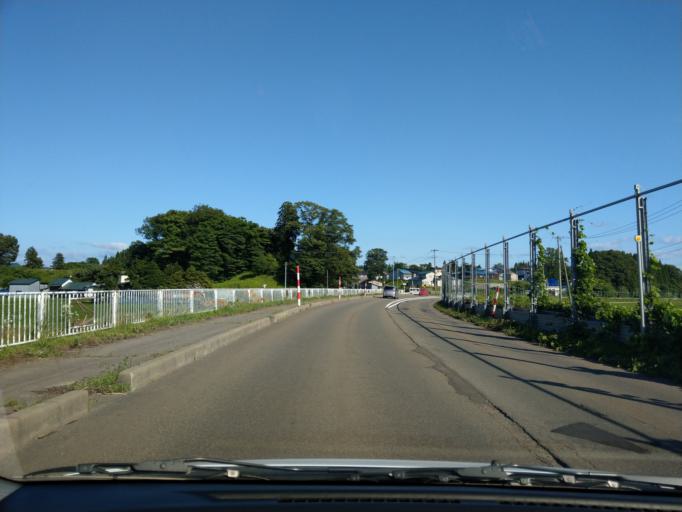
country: JP
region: Akita
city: Takanosu
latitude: 40.1932
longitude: 140.3996
